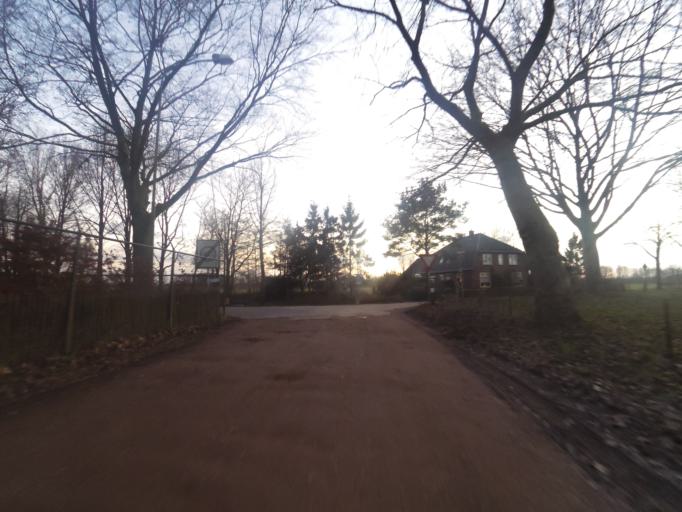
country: NL
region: Gelderland
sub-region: Gemeente Doetinchem
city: Doetinchem
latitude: 51.9363
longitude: 6.3270
